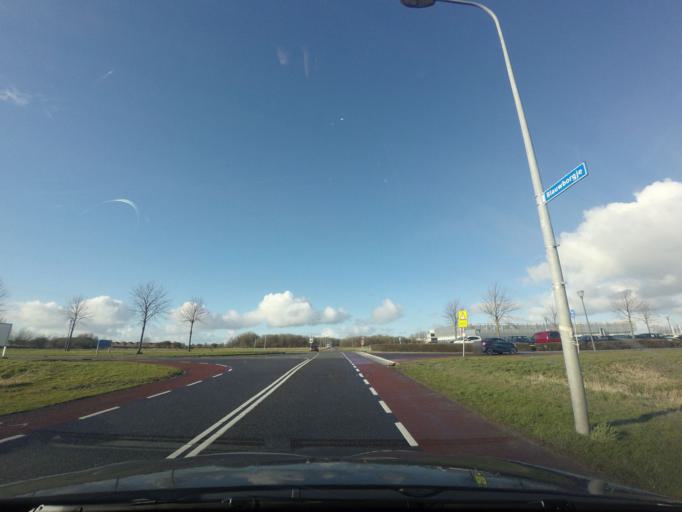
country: NL
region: Groningen
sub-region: Gemeente Groningen
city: Korrewegwijk
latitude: 53.2439
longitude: 6.5272
